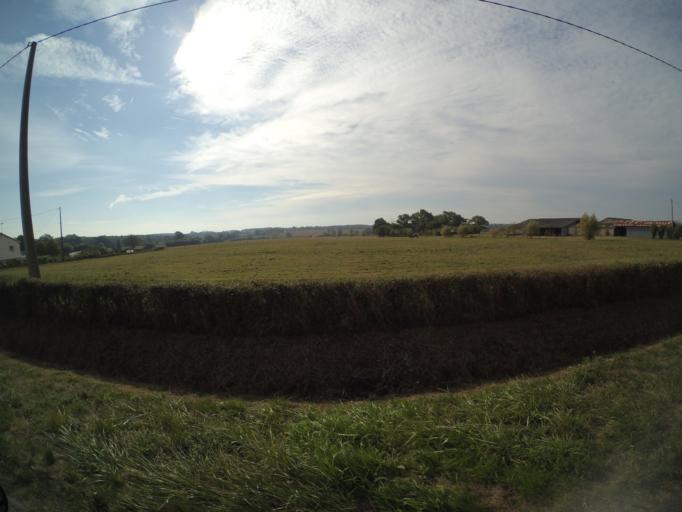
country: FR
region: Pays de la Loire
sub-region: Departement de Maine-et-Loire
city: Geste
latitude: 47.1814
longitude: -1.0927
